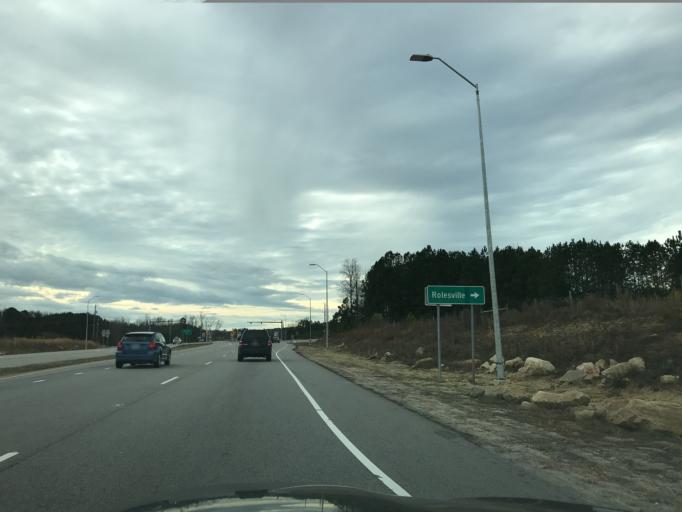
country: US
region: North Carolina
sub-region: Wake County
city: Rolesville
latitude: 35.9149
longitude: -78.4487
